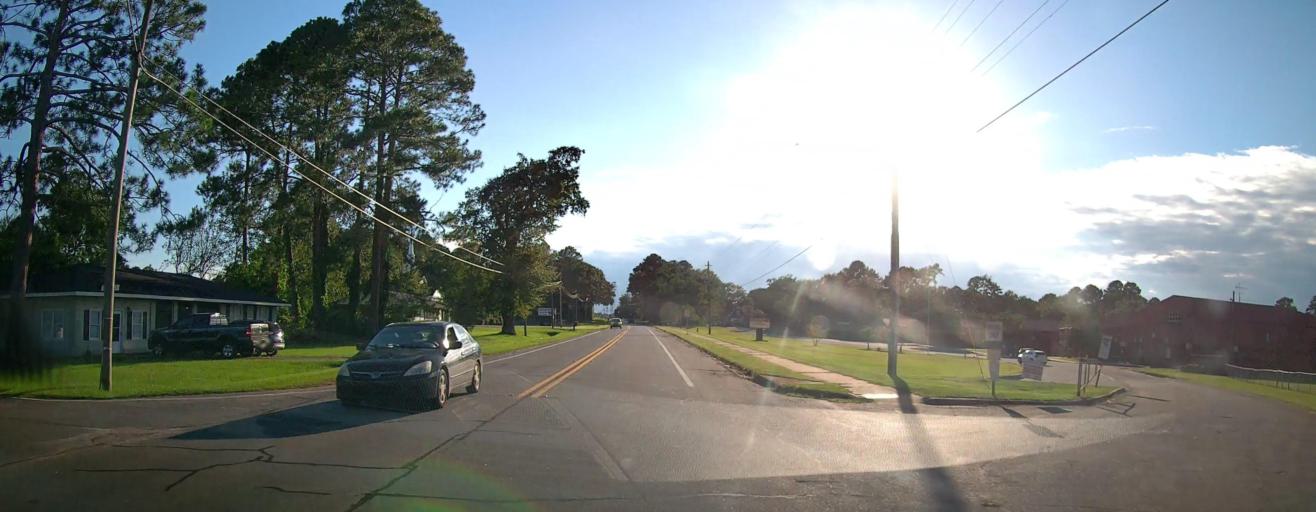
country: US
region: Georgia
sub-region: Pulaski County
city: Hawkinsville
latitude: 32.2813
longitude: -83.4824
